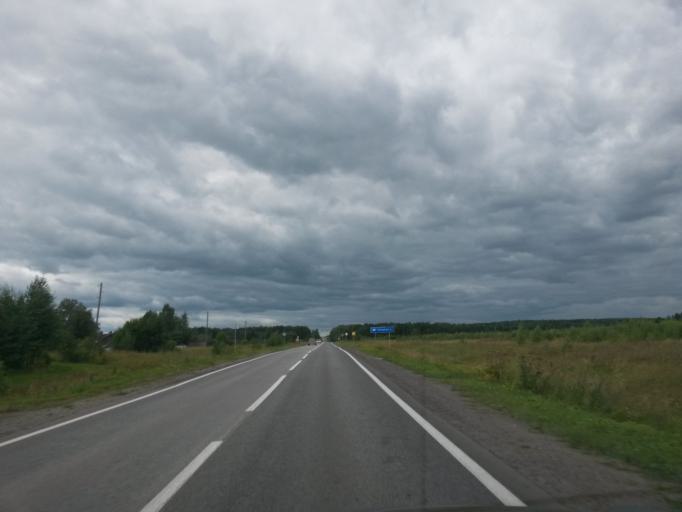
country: RU
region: Jaroslavl
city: Konstantinovskiy
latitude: 57.8116
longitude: 39.7293
